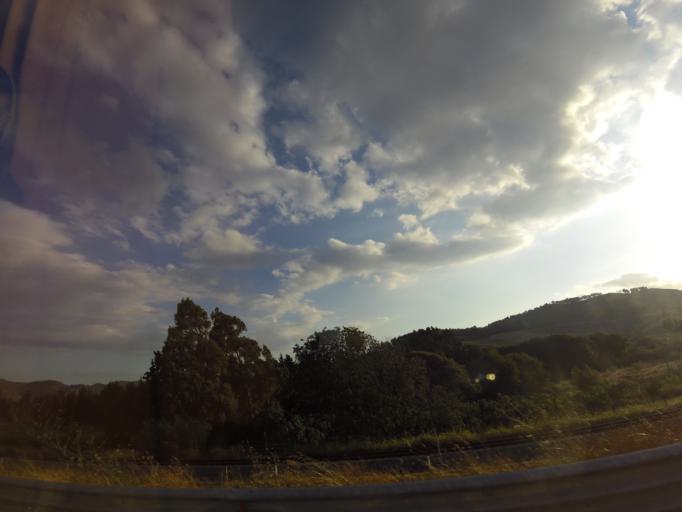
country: IT
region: Calabria
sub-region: Provincia di Catanzaro
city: Catanzaro
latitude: 38.8753
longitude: 16.5576
